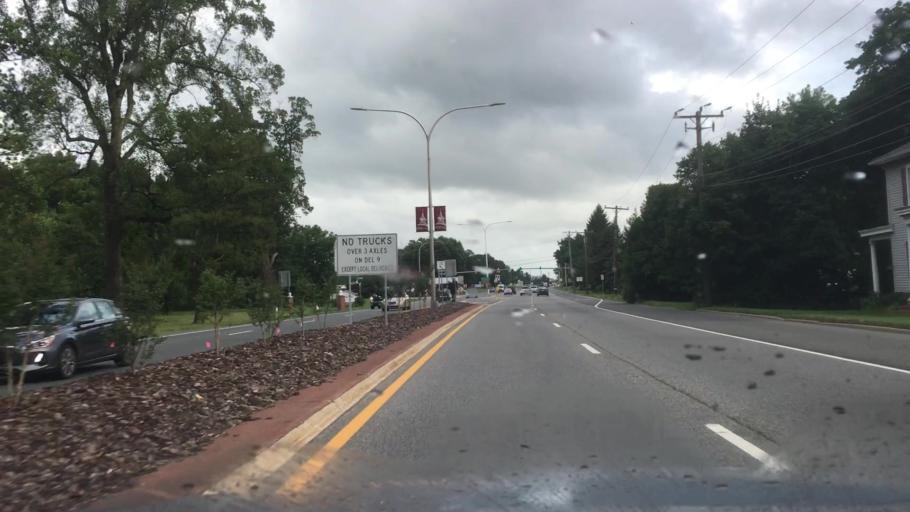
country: US
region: Delaware
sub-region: Kent County
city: Smyrna
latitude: 39.2932
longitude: -75.5975
